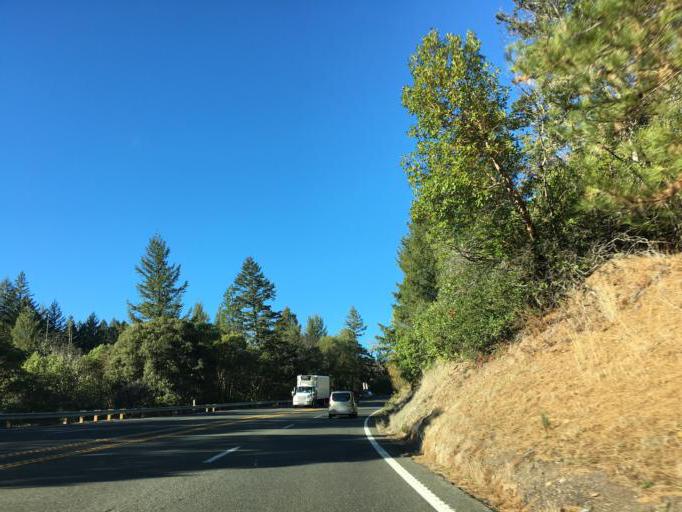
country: US
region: California
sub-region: Mendocino County
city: Laytonville
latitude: 39.6190
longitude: -123.4645
